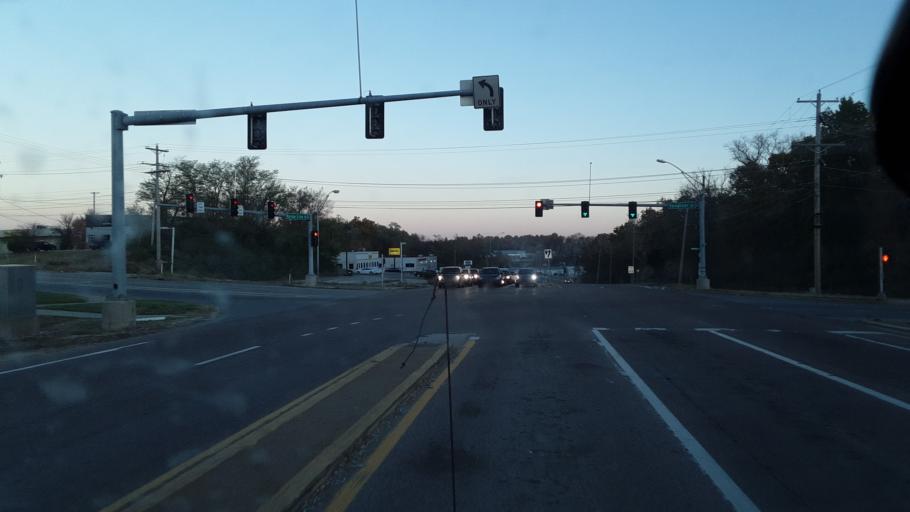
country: US
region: Missouri
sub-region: Boone County
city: Columbia
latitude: 38.9707
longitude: -92.3255
